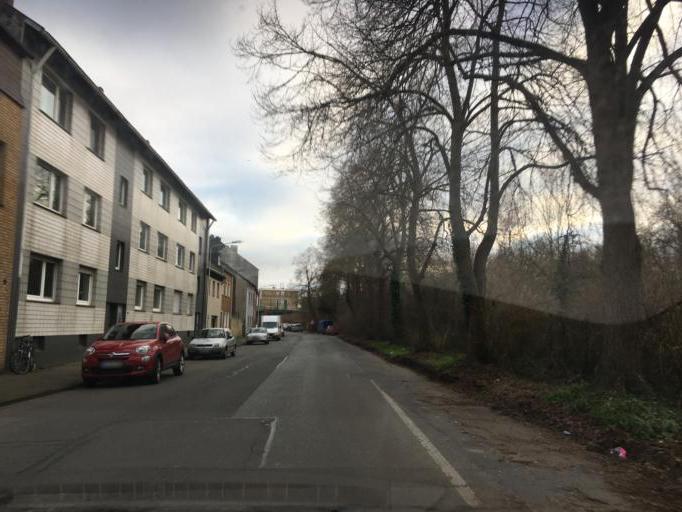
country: DE
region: North Rhine-Westphalia
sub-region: Regierungsbezirk Koln
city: Dueren
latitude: 50.8032
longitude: 6.4683
